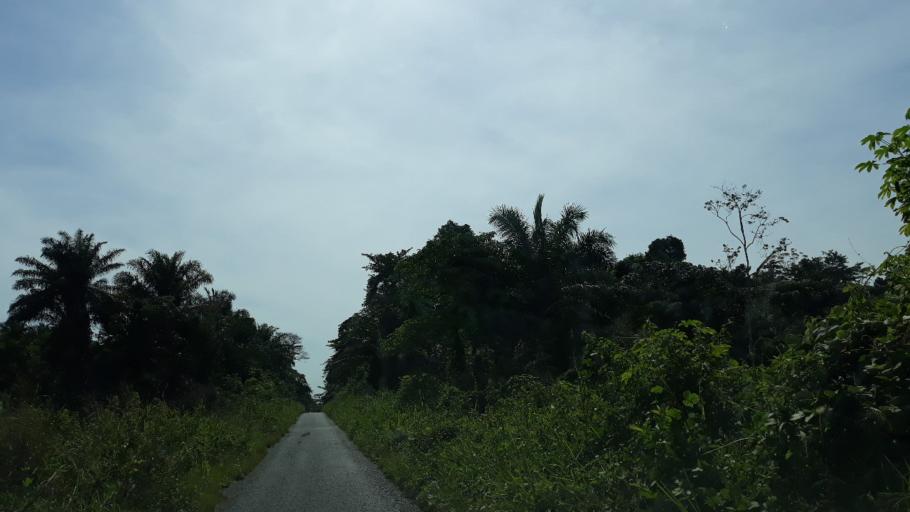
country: CD
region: Maniema
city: Kindu
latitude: -2.9051
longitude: 26.0336
